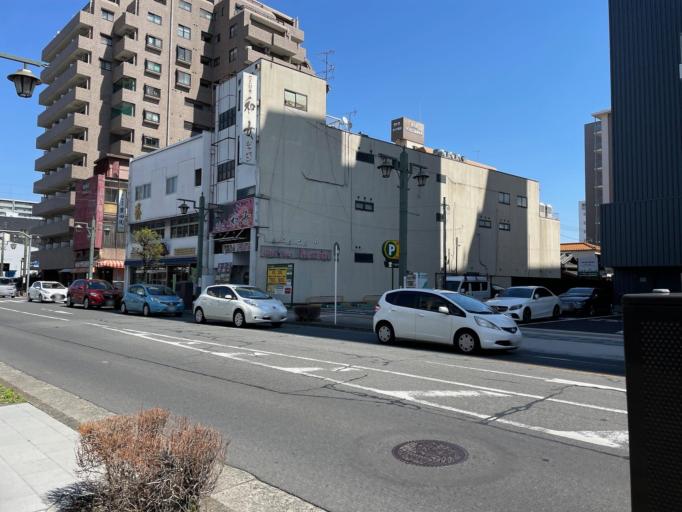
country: JP
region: Gunma
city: Takasaki
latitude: 36.3262
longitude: 139.0069
